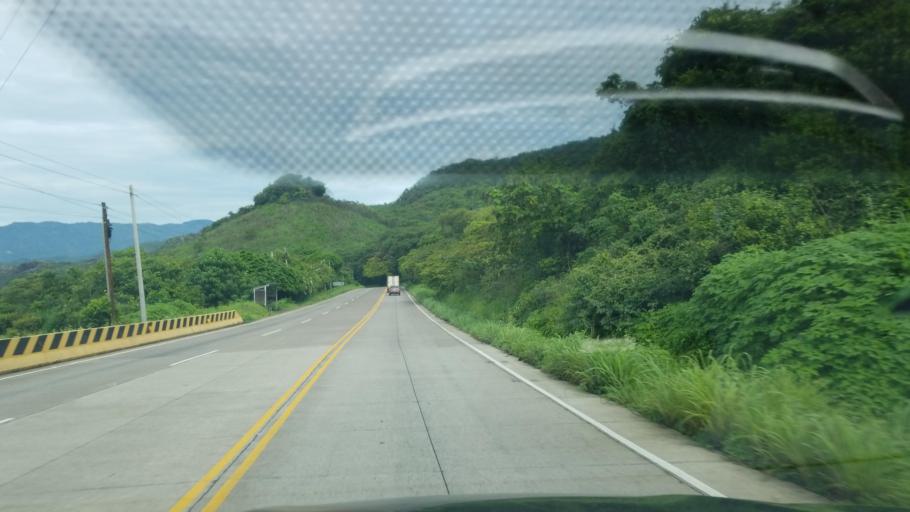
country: HN
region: Francisco Morazan
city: El Porvenir
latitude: 13.6999
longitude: -87.3188
